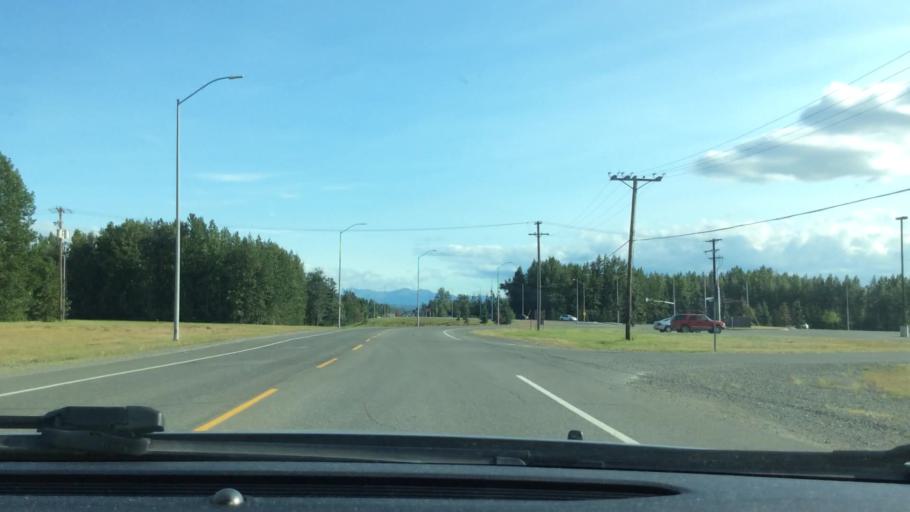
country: US
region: Alaska
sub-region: Anchorage Municipality
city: Anchorage
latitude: 61.2424
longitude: -149.7786
